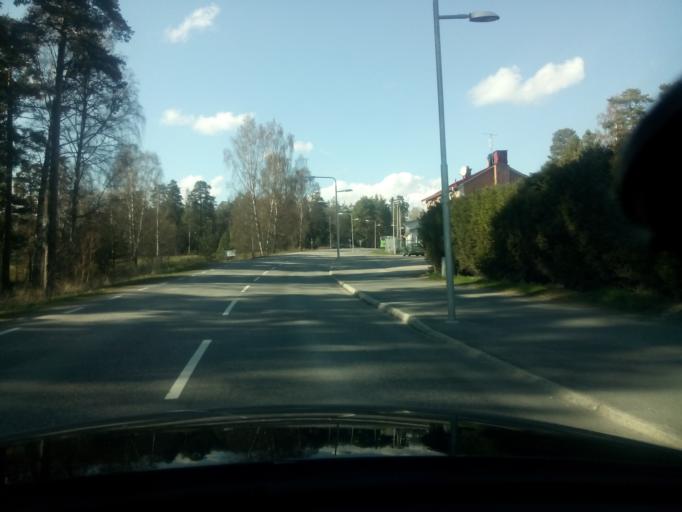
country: SE
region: Soedermanland
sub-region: Flens Kommun
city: Malmkoping
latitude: 59.1395
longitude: 16.7191
